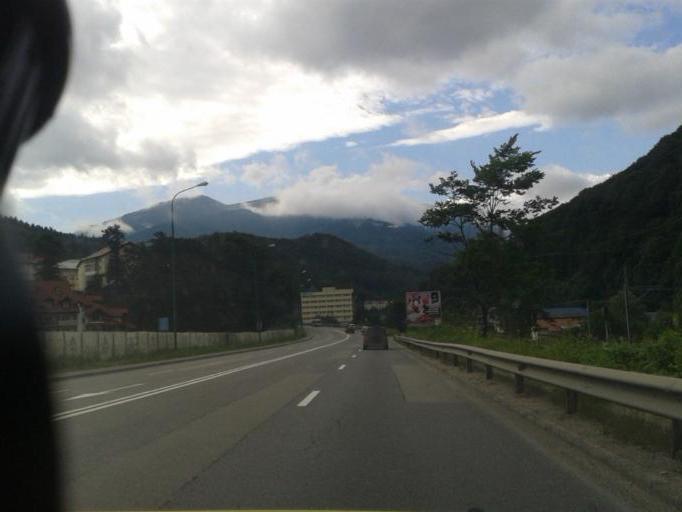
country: RO
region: Prahova
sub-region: Oras Sinaia
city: Sinaia
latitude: 45.3317
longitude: 25.5616
